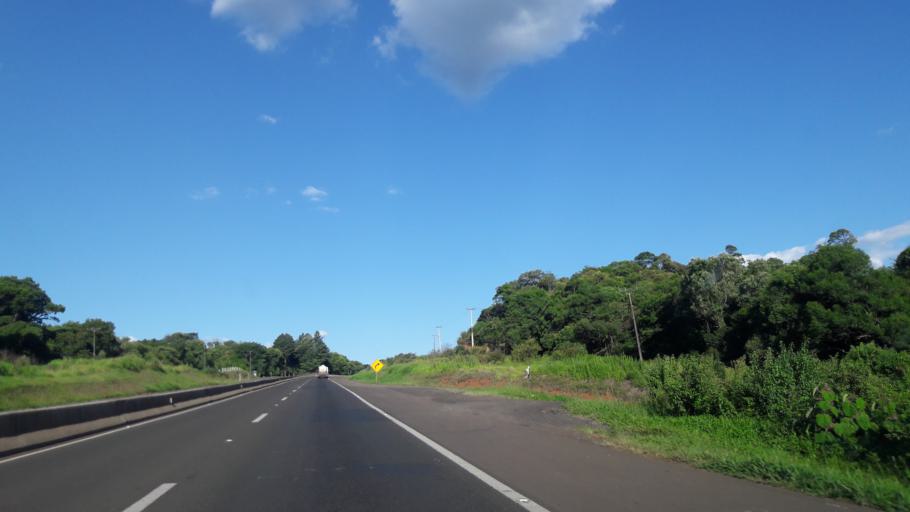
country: BR
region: Parana
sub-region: Guarapuava
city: Guarapuava
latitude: -25.3454
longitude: -51.4037
